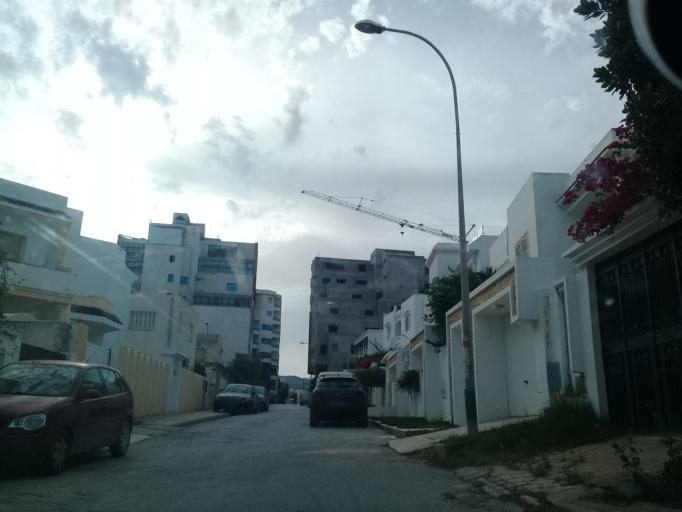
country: TN
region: Ariana
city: Ariana
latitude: 36.8676
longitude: 10.1728
